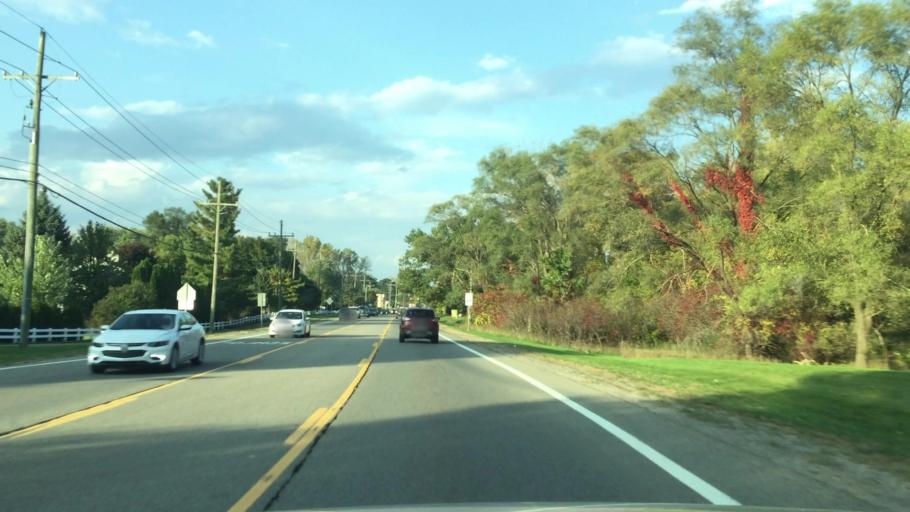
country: US
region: Michigan
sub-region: Oakland County
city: Keego Harbor
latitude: 42.6241
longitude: -83.3969
